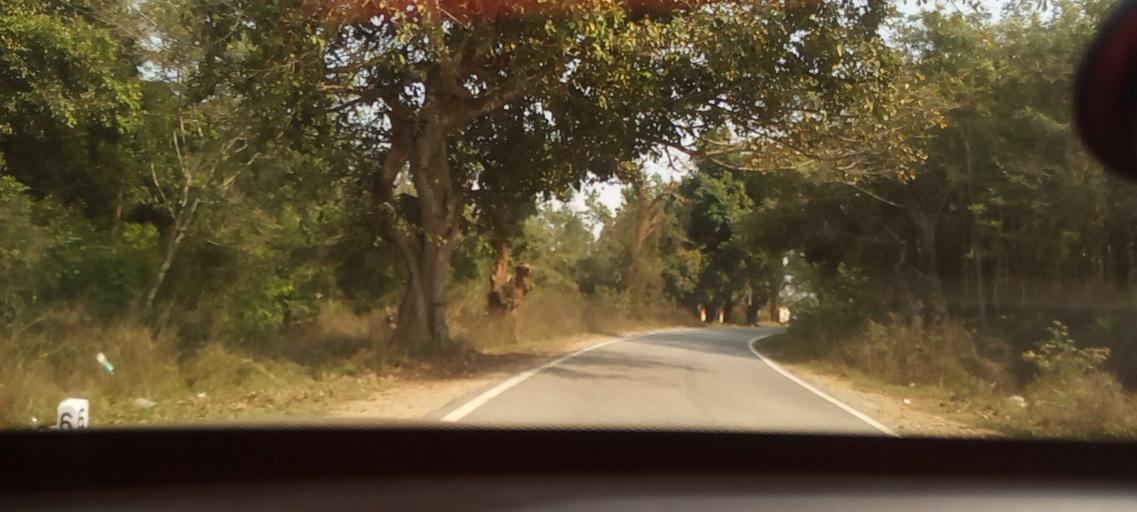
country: IN
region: Karnataka
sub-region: Hassan
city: Belur
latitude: 13.1869
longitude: 75.7994
